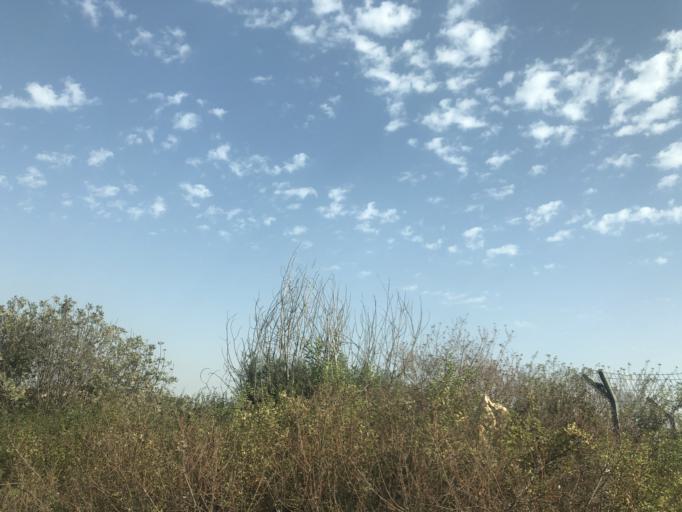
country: IL
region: Central District
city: Rosh Ha'Ayin
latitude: 32.0833
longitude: 34.9442
